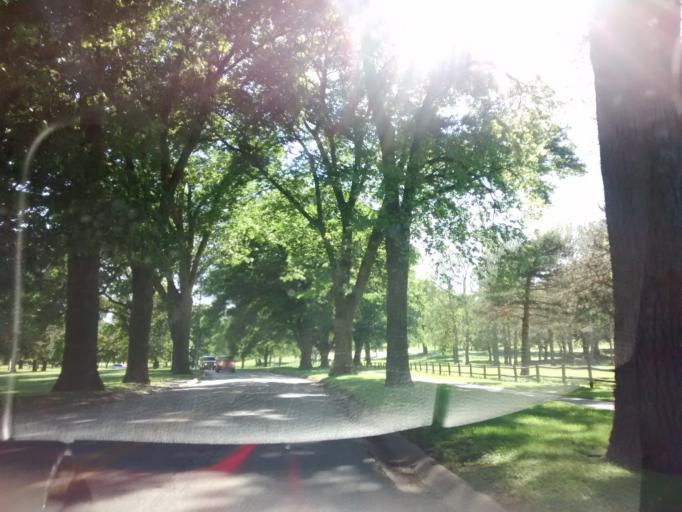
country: US
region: Nebraska
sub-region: Douglas County
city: Ralston
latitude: 41.2527
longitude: -96.0112
